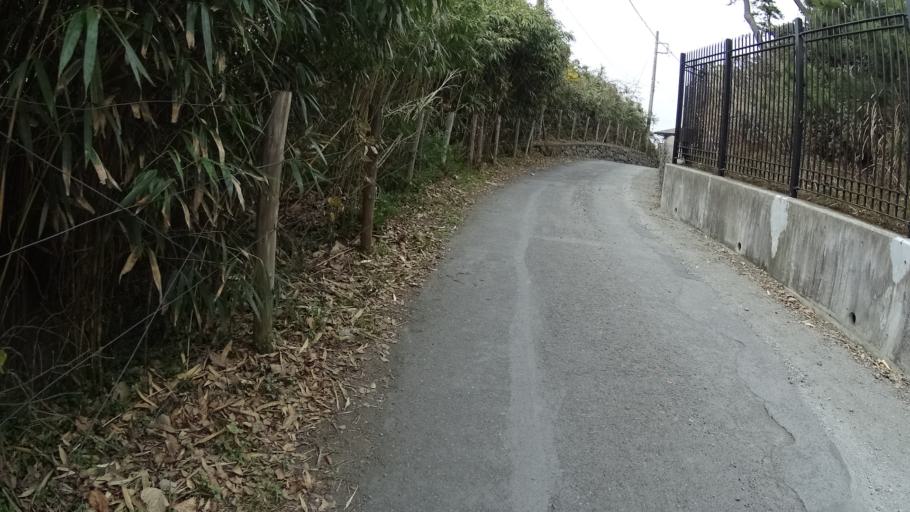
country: JP
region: Kanagawa
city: Oiso
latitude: 35.3024
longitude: 139.2892
